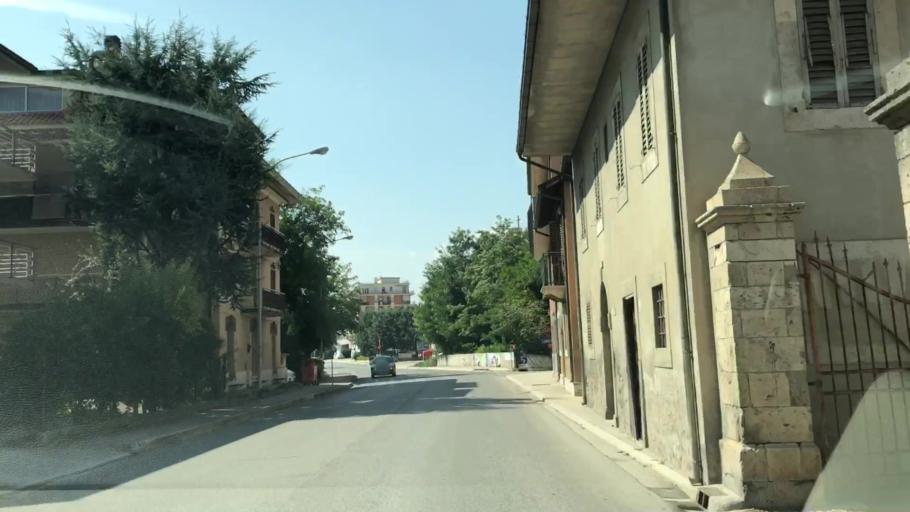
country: IT
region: The Marches
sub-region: Provincia di Ascoli Piceno
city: Stella
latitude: 42.8877
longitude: 13.8119
